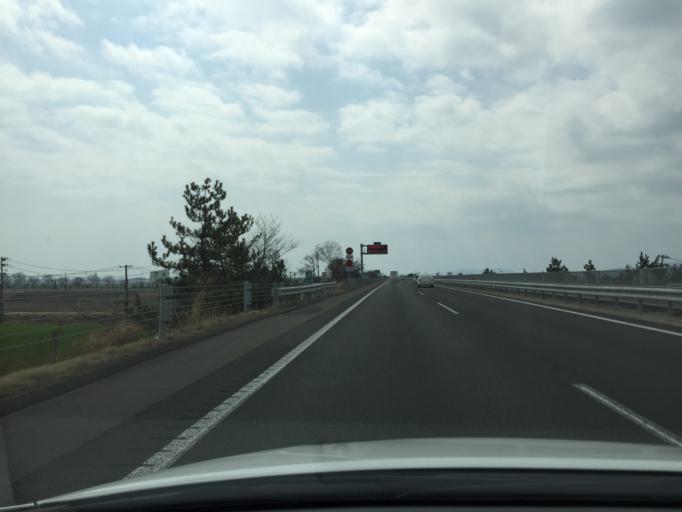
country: JP
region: Miyagi
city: Iwanuma
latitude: 38.1417
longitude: 140.8907
